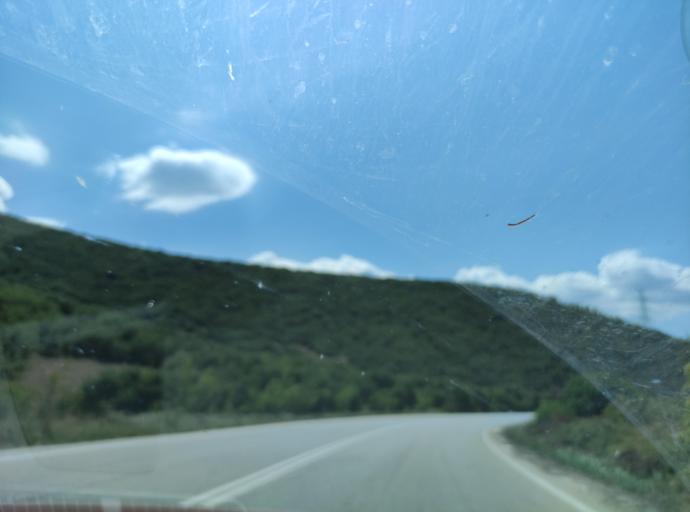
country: GR
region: East Macedonia and Thrace
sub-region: Nomos Kavalas
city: Nikisiani
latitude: 40.9877
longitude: 24.0965
